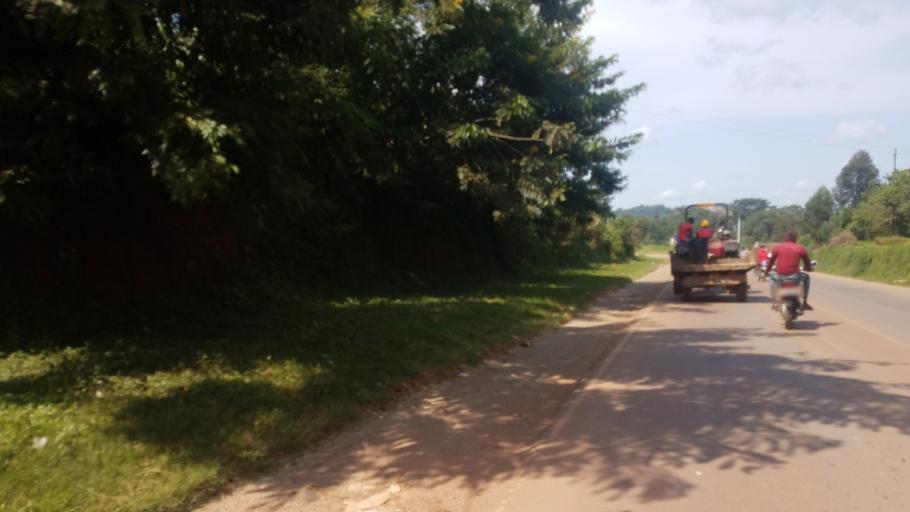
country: UG
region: Central Region
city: Masaka
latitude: -0.3347
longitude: 31.7204
